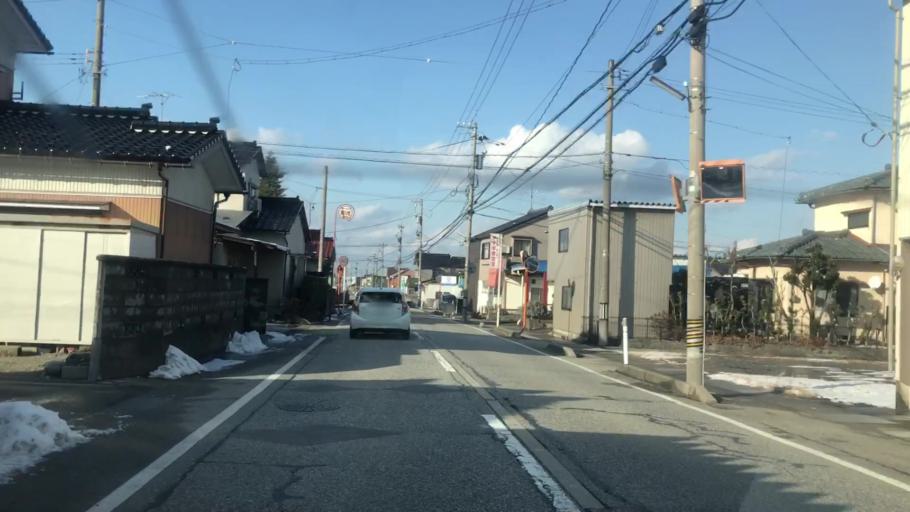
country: JP
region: Toyama
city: Toyama-shi
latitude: 36.6767
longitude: 137.2738
